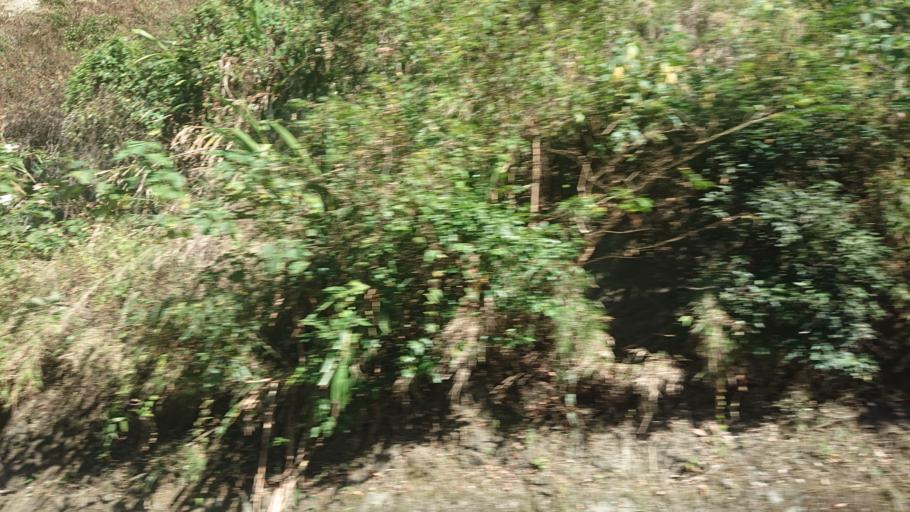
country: TW
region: Taiwan
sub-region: Chiayi
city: Jiayi Shi
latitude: 23.5271
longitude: 120.6294
